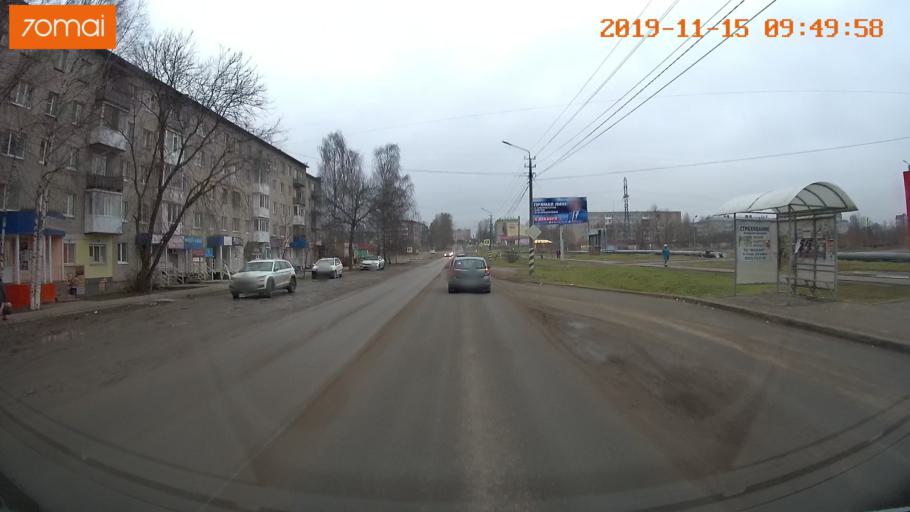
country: RU
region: Vologda
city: Sheksna
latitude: 59.2303
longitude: 38.5130
